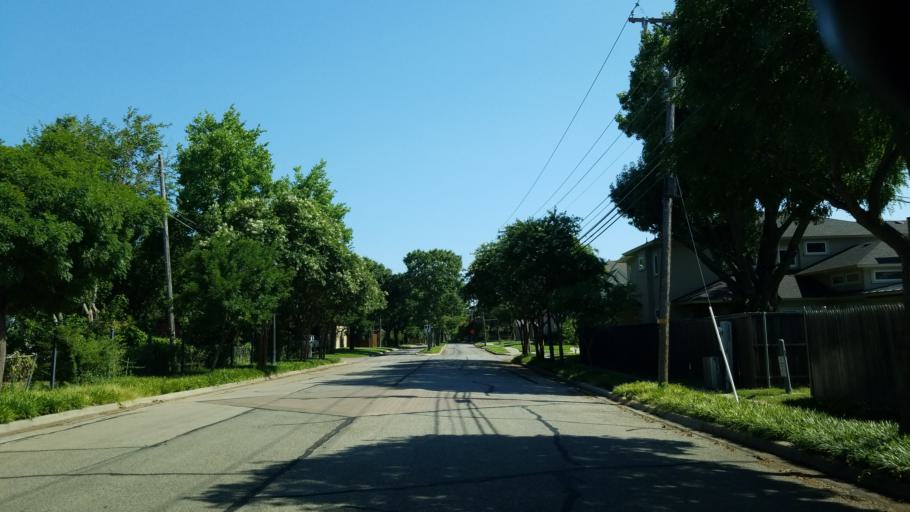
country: US
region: Texas
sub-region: Dallas County
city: Farmers Branch
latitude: 32.9209
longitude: -96.8875
